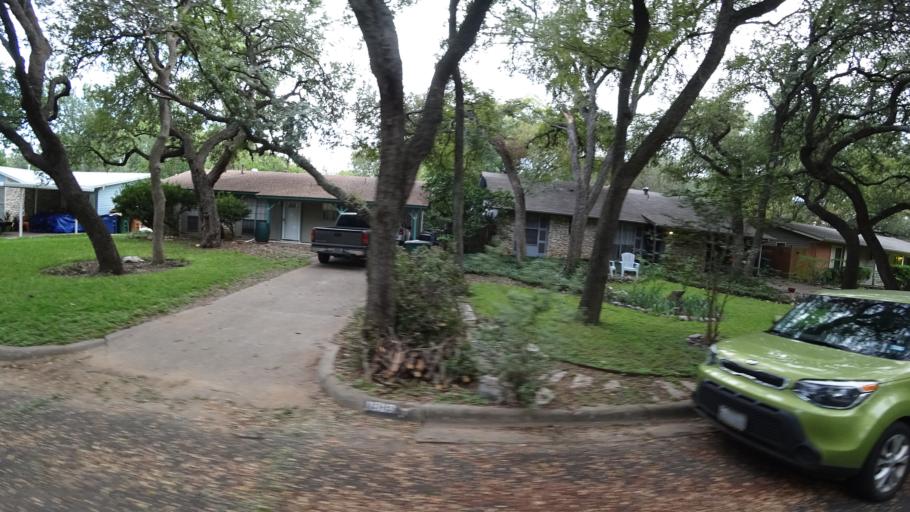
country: US
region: Texas
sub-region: Travis County
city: Rollingwood
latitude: 30.2188
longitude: -97.7940
